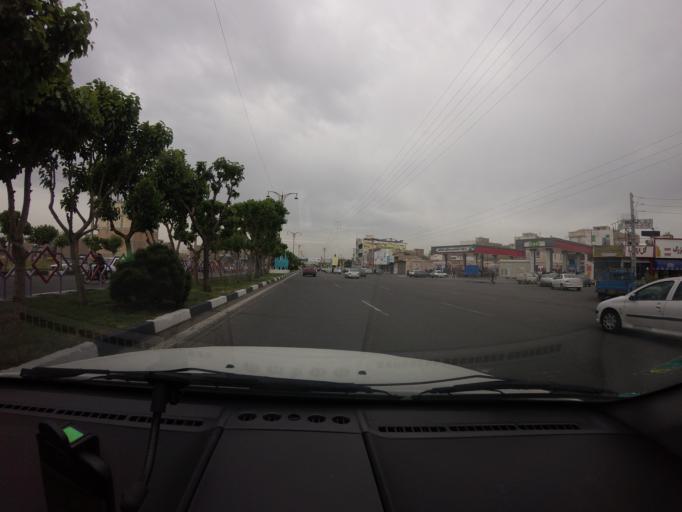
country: IR
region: Tehran
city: Eslamshahr
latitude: 35.5482
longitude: 51.2247
